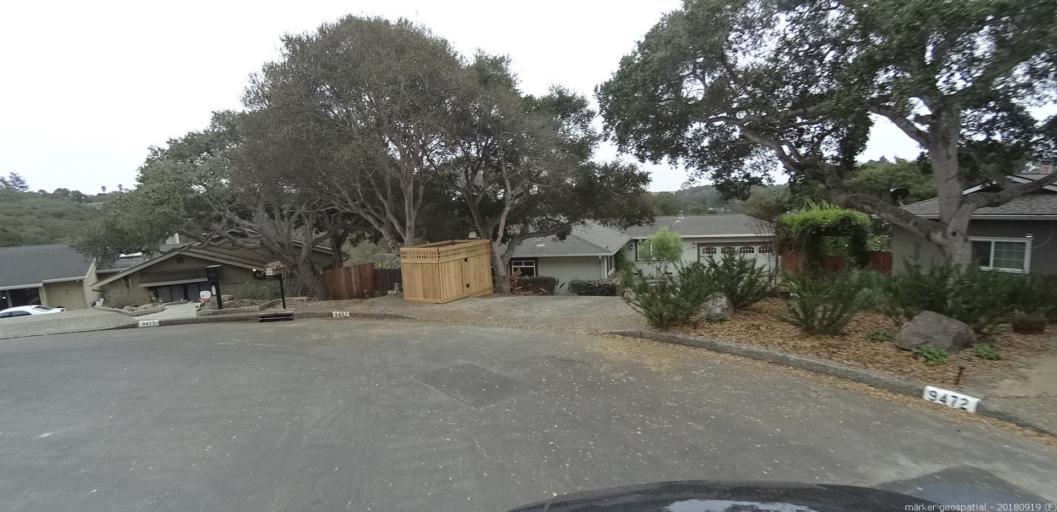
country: US
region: California
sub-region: Monterey County
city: Castroville
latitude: 36.7803
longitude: -121.7153
